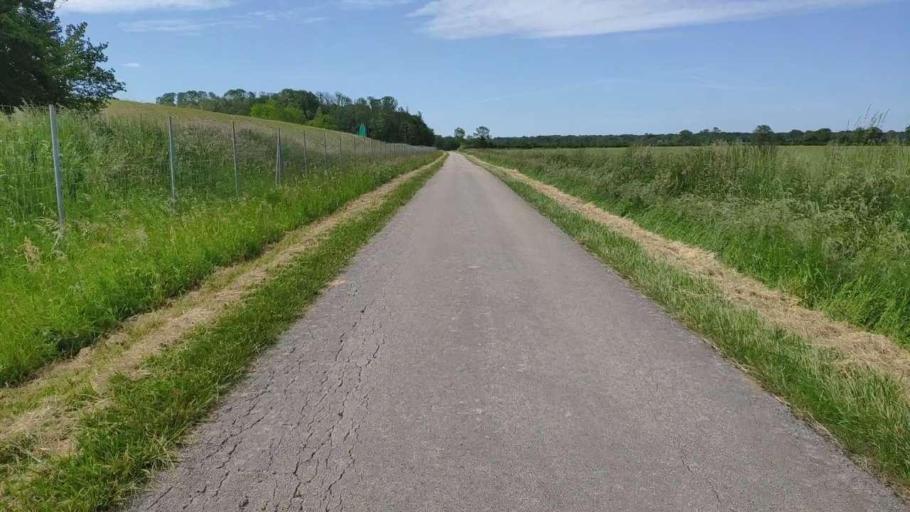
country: FR
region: Franche-Comte
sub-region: Departement du Jura
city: Bletterans
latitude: 46.6865
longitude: 5.4286
